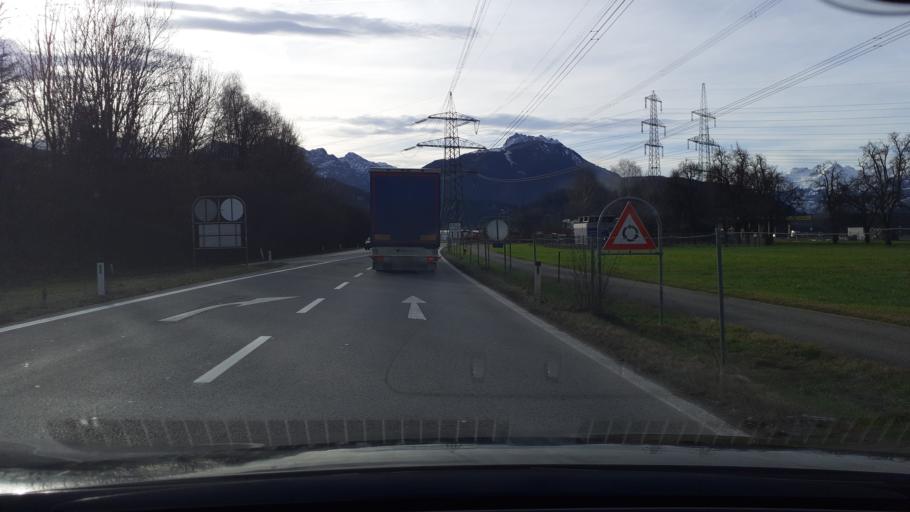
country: AT
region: Vorarlberg
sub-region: Politischer Bezirk Feldkirch
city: Rankweil
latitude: 47.2746
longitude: 9.6212
